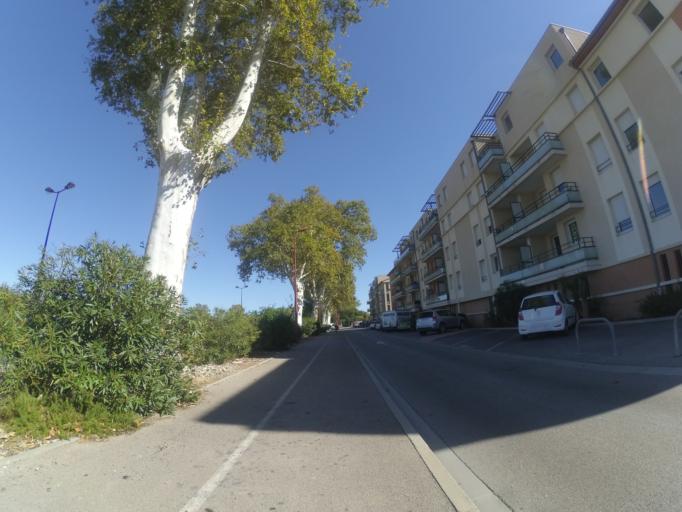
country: FR
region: Languedoc-Roussillon
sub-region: Departement des Pyrenees-Orientales
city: Saint-Esteve
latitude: 42.7103
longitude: 2.8560
